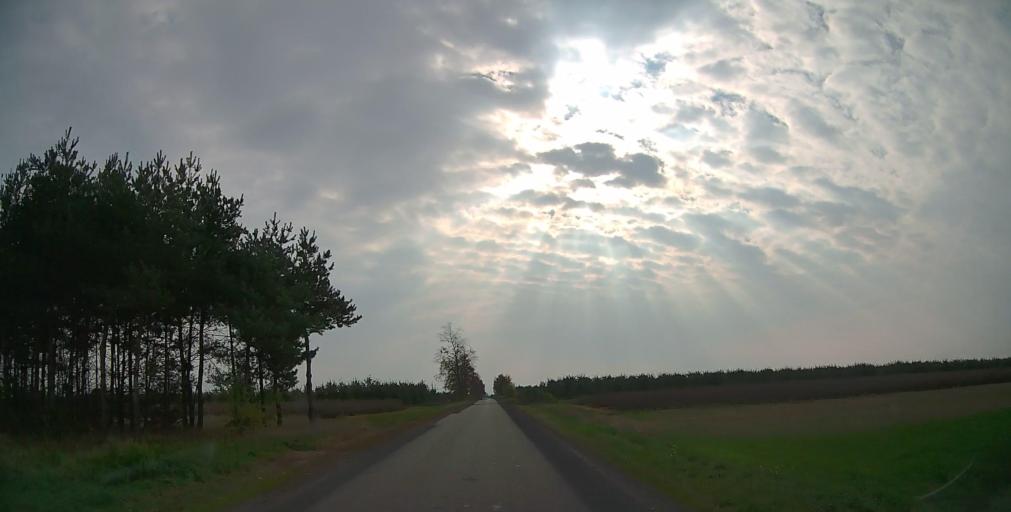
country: PL
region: Masovian Voivodeship
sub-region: Powiat grojecki
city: Mogielnica
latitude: 51.6540
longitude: 20.7217
